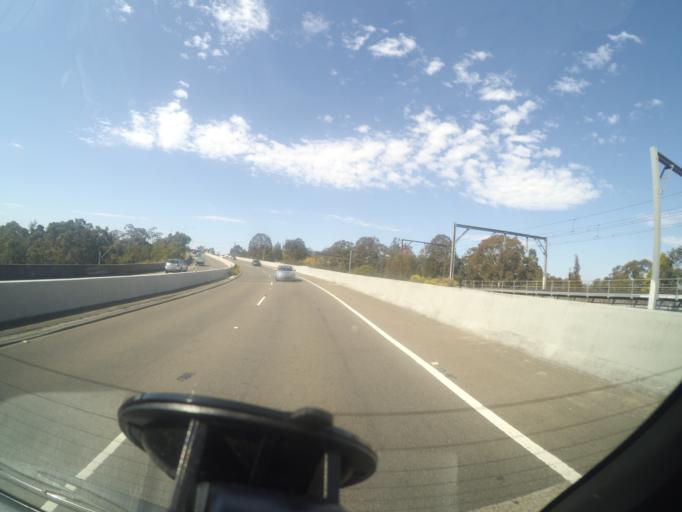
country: AU
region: New South Wales
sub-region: Blue Mountains Municipality
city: Blaxland
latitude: -33.7215
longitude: 150.5948
